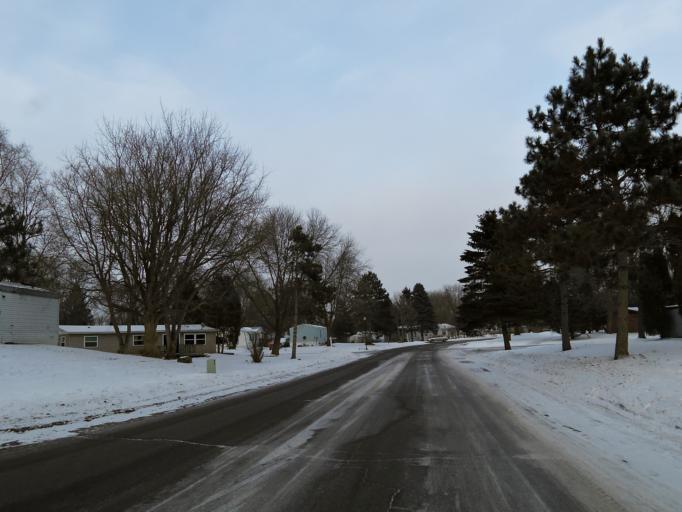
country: US
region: Minnesota
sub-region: Washington County
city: Lake Elmo
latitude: 44.9619
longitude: -92.8769
